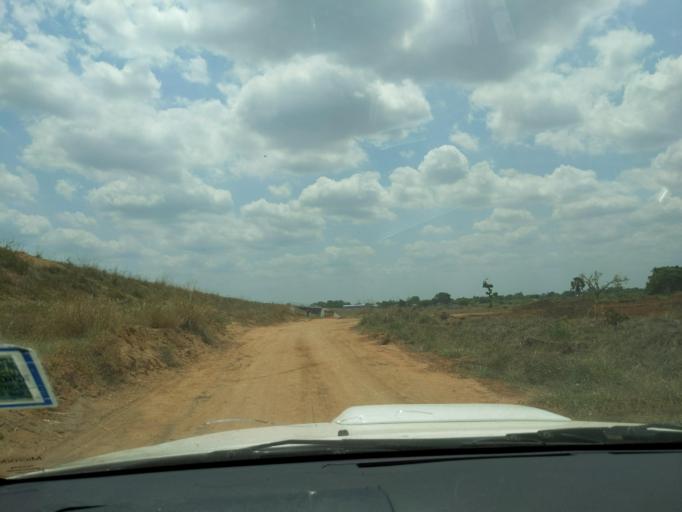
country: MZ
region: Zambezia
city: Quelimane
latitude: -17.2568
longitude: 37.0742
